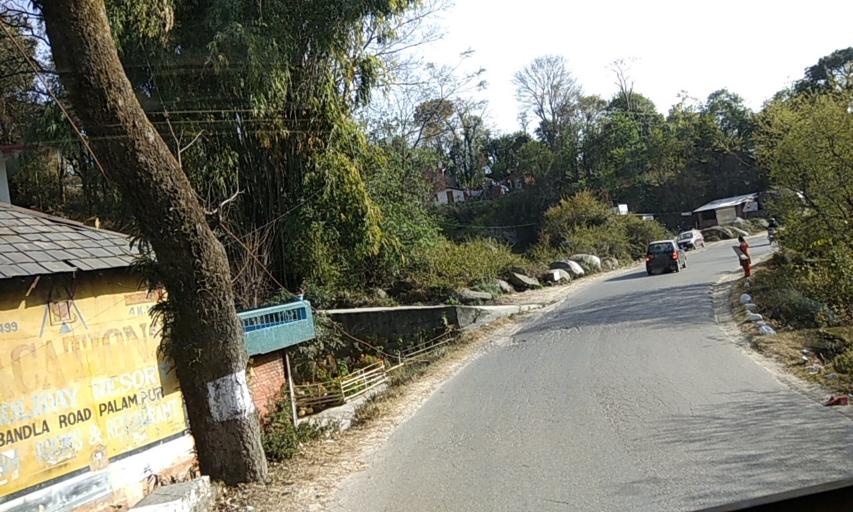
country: IN
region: Himachal Pradesh
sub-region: Kangra
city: Palampur
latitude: 32.0853
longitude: 76.5217
